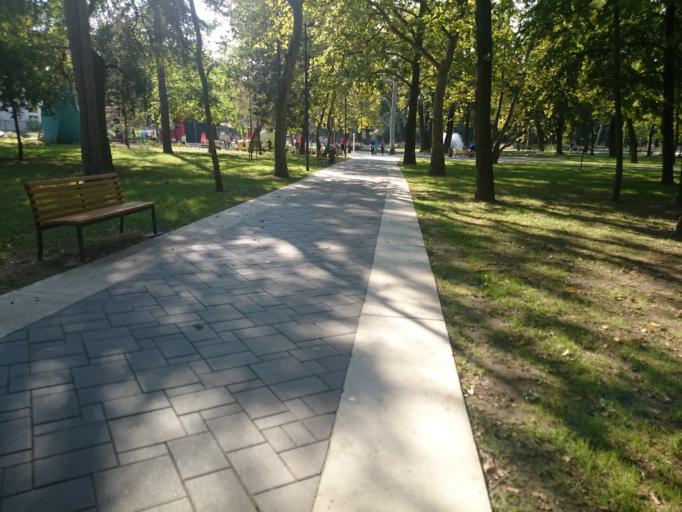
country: HU
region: Hajdu-Bihar
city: Debrecen
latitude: 47.5530
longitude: 21.6272
